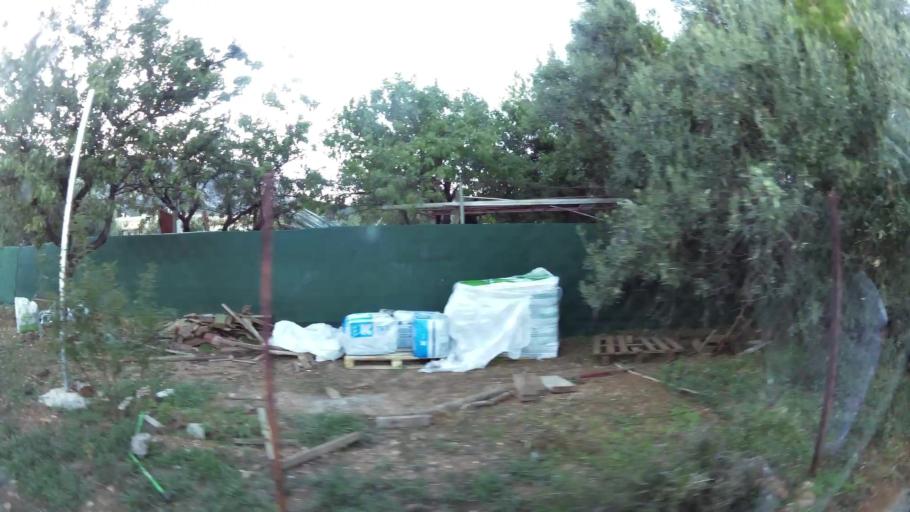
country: GR
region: Attica
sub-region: Nomarchia Anatolikis Attikis
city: Paiania
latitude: 37.9709
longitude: 23.8411
